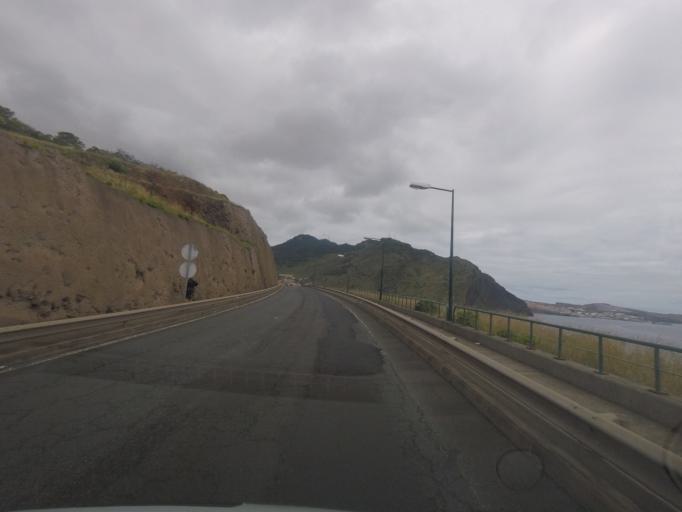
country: PT
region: Madeira
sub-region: Machico
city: Machico
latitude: 32.7103
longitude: -16.7616
